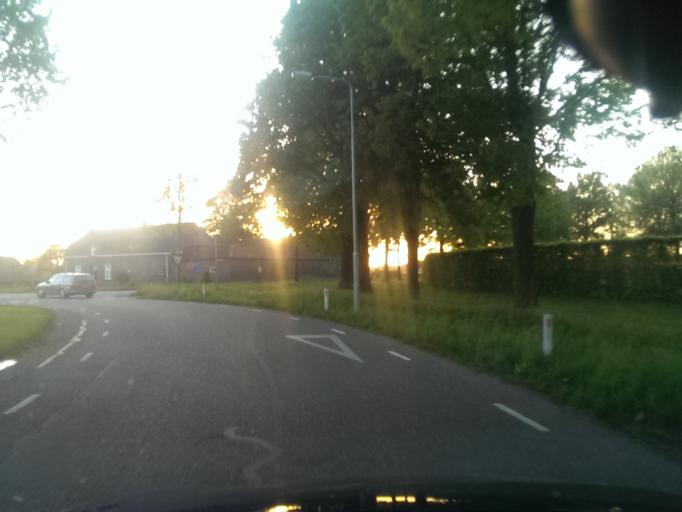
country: NL
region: Limburg
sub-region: Gemeente Nederweert
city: Nederweert
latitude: 51.2895
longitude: 5.7695
